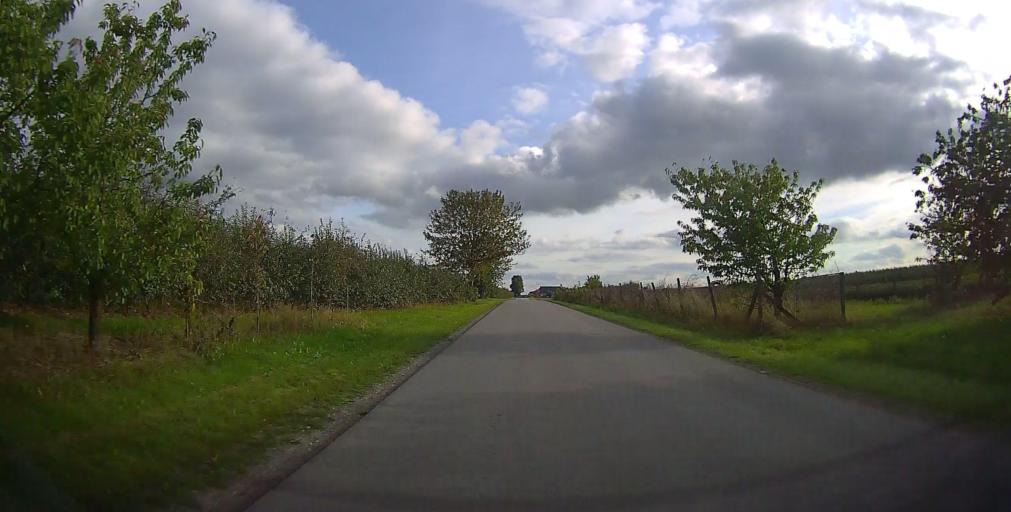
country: PL
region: Masovian Voivodeship
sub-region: Powiat bialobrzeski
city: Promna
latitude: 51.7446
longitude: 20.9644
